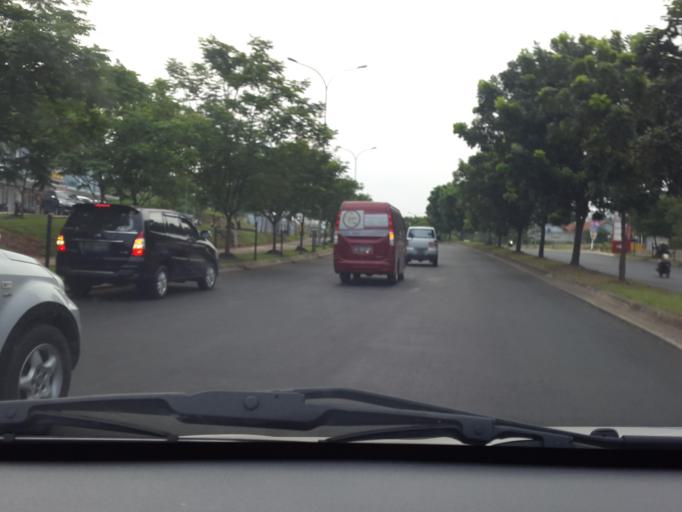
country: ID
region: Banten
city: South Tangerang
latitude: -6.2748
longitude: 106.7044
